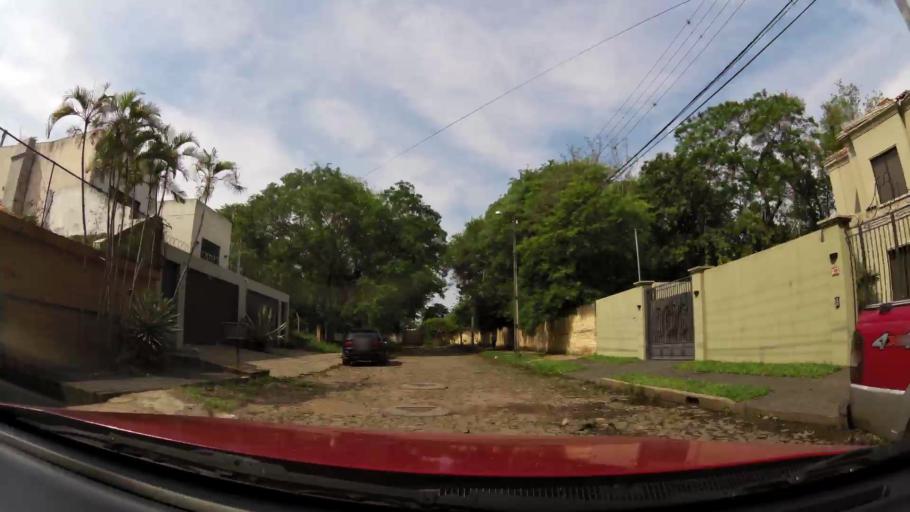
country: PY
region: Asuncion
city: Asuncion
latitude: -25.2678
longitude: -57.5640
